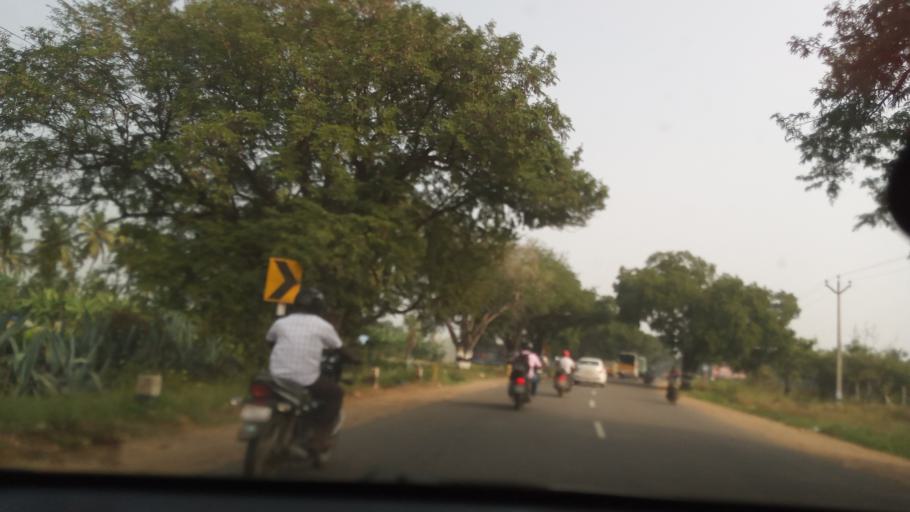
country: IN
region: Tamil Nadu
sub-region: Coimbatore
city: Annur
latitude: 11.1598
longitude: 77.0508
